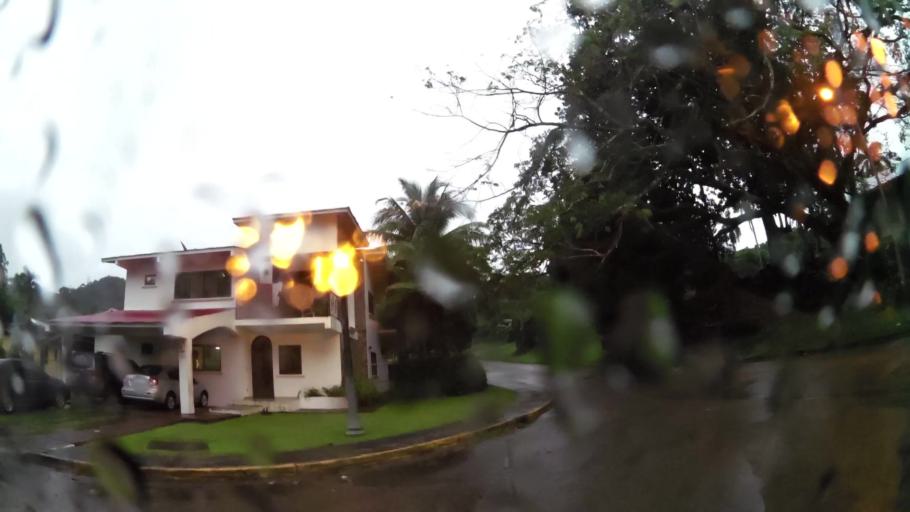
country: PA
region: Panama
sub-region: Distrito de Panama
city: Paraiso
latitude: 9.0314
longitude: -79.6256
